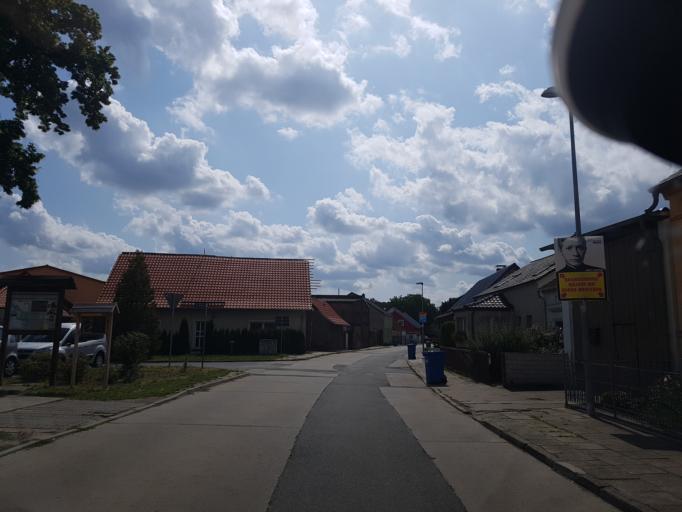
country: DE
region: Brandenburg
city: Gross Kreutz
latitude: 52.3369
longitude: 12.7264
